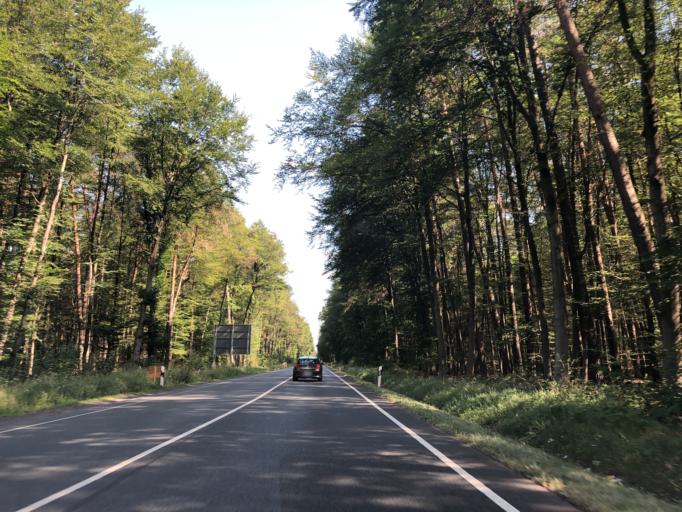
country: DE
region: Hesse
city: Heusenstamm
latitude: 50.0520
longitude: 8.7507
